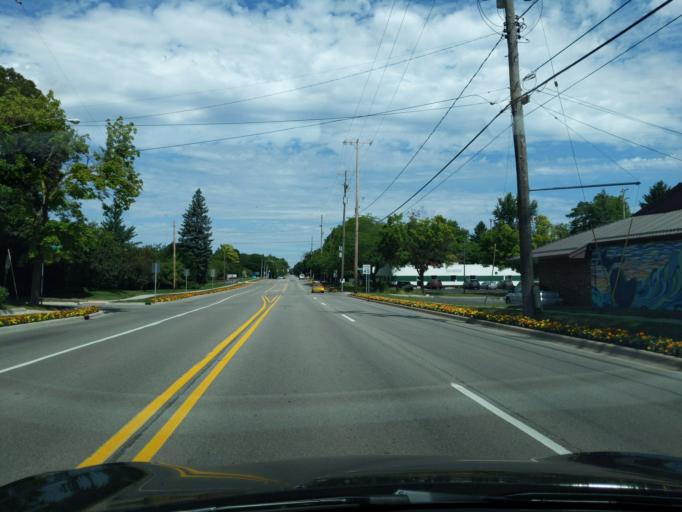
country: US
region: Michigan
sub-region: Midland County
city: Midland
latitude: 43.6220
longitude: -84.2470
